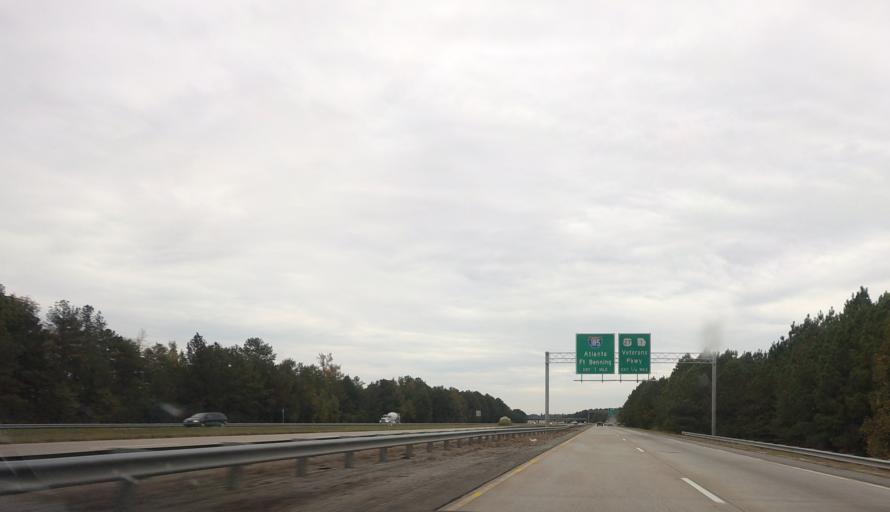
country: US
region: Alabama
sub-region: Russell County
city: Phenix City
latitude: 32.5508
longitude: -84.9419
